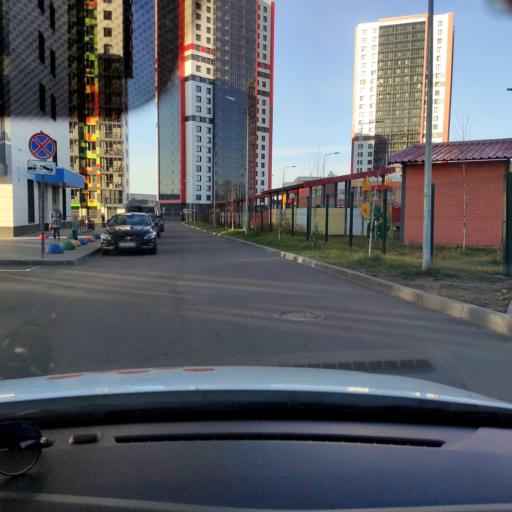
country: RU
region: Tatarstan
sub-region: Gorod Kazan'
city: Kazan
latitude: 55.7630
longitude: 49.1942
